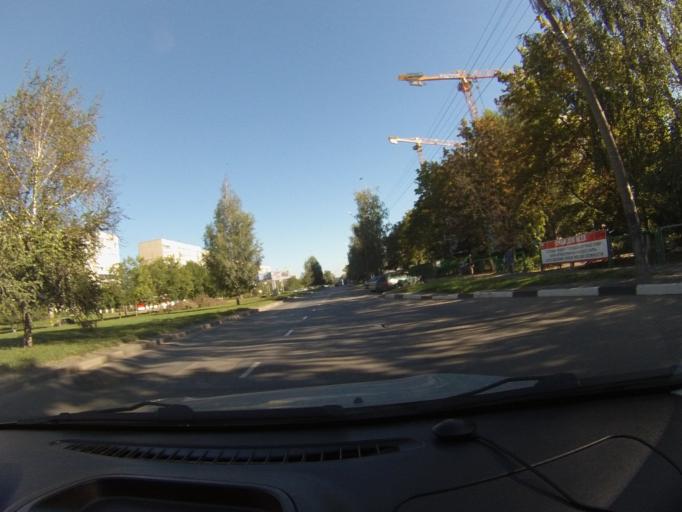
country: RU
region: Tambov
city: Tambov
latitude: 52.7642
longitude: 41.4207
